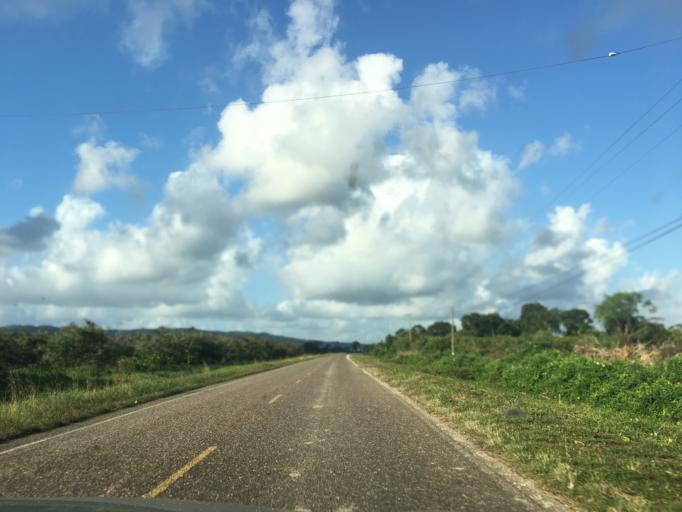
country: BZ
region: Stann Creek
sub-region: Dangriga
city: Dangriga
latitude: 16.8059
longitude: -88.3794
